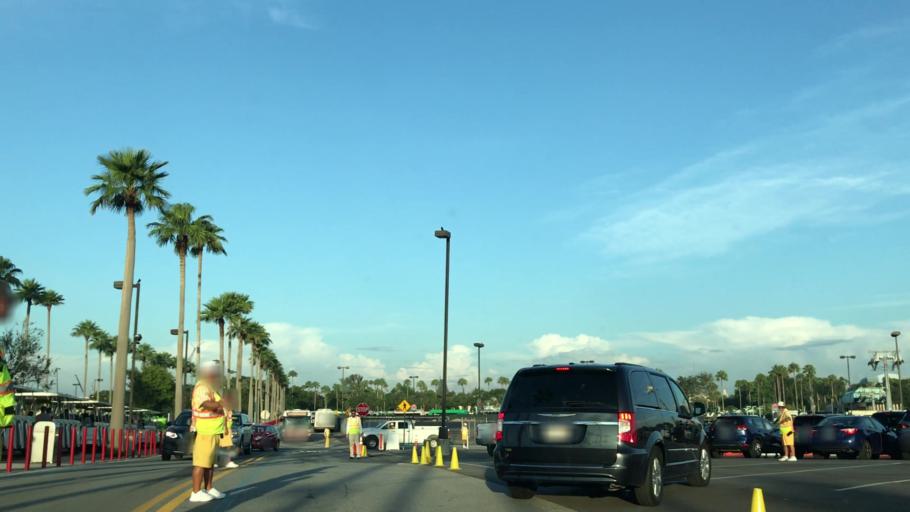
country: US
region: Florida
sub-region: Osceola County
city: Celebration
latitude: 28.3588
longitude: -81.5539
